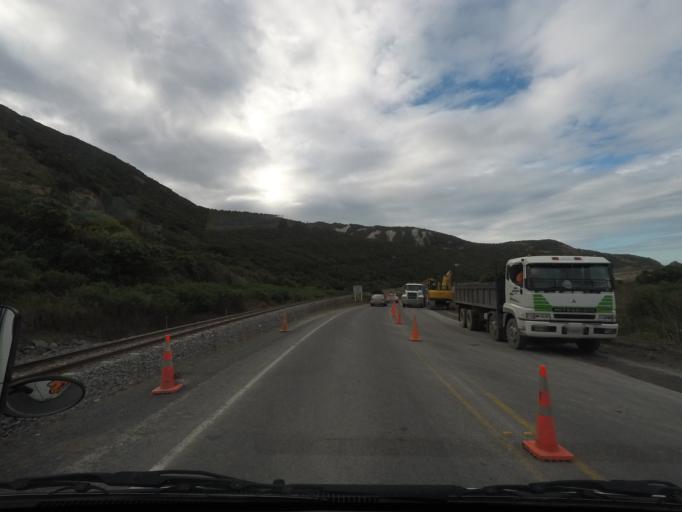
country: NZ
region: Canterbury
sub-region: Kaikoura District
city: Kaikoura
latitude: -42.2186
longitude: 173.8577
